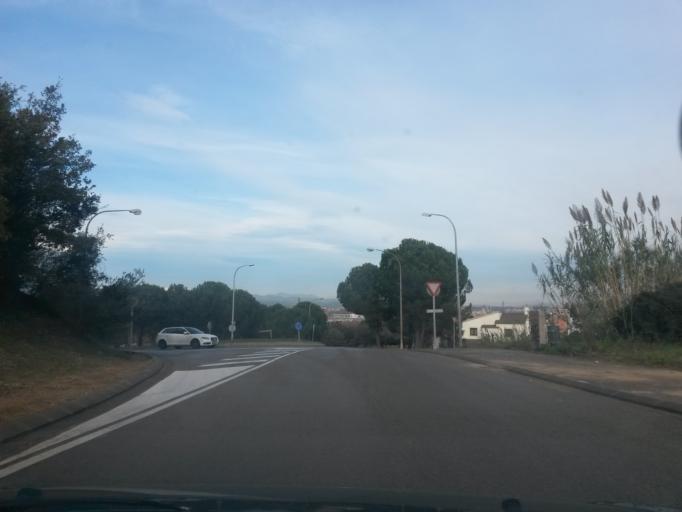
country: ES
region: Catalonia
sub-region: Provincia de Girona
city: Salt
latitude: 41.9595
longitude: 2.8138
